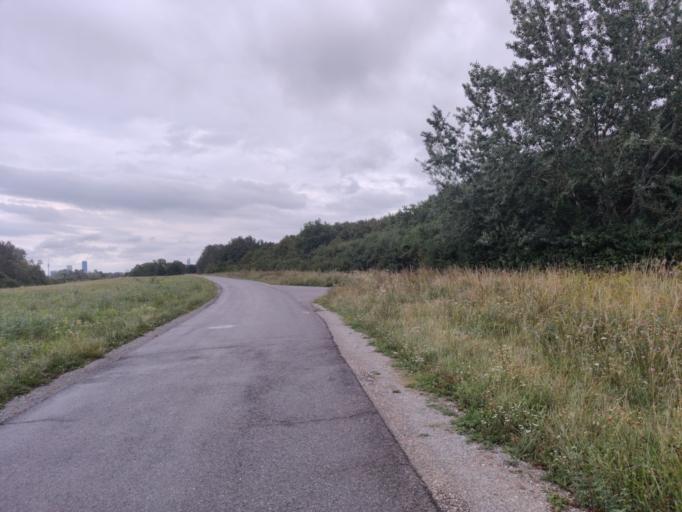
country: AT
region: Lower Austria
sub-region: Politischer Bezirk Korneuburg
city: Langenzersdorf
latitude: 48.2892
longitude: 16.3524
